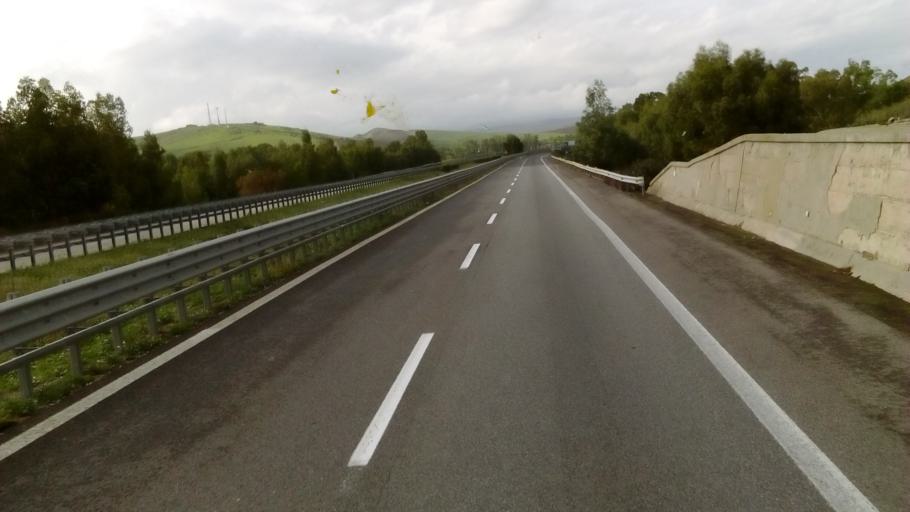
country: IT
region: Sicily
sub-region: Catania
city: Raddusa
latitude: 37.5437
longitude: 14.5580
